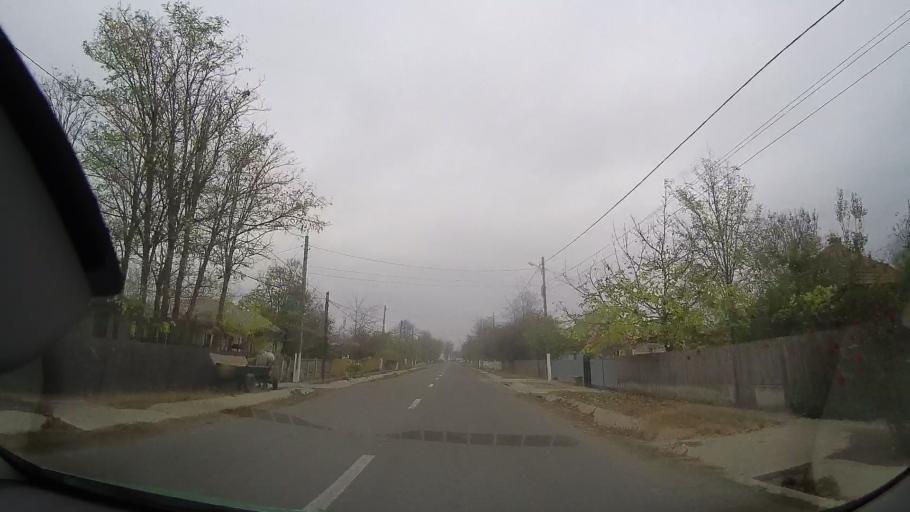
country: RO
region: Braila
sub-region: Comuna Rosiori
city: Rosiori
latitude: 44.8122
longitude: 27.3889
